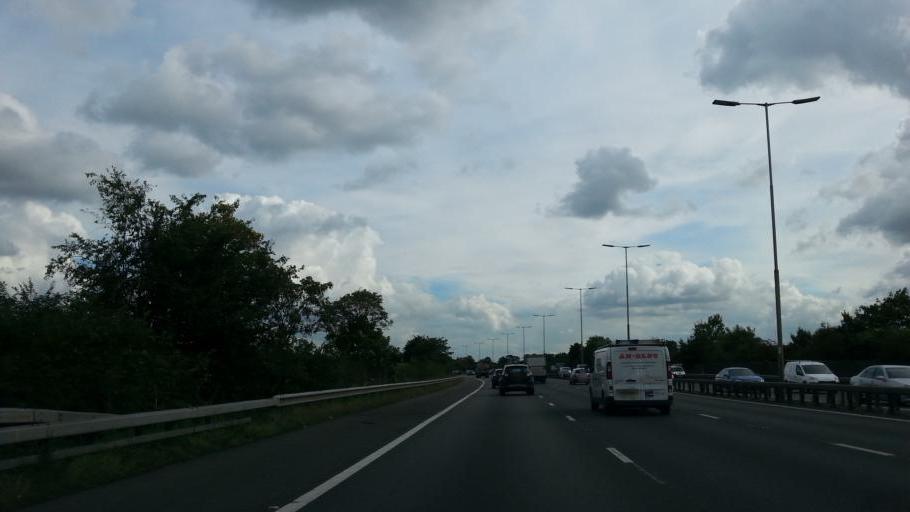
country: GB
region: England
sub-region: Royal Borough of Windsor and Maidenhead
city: Datchet
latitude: 51.4927
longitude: -0.5824
